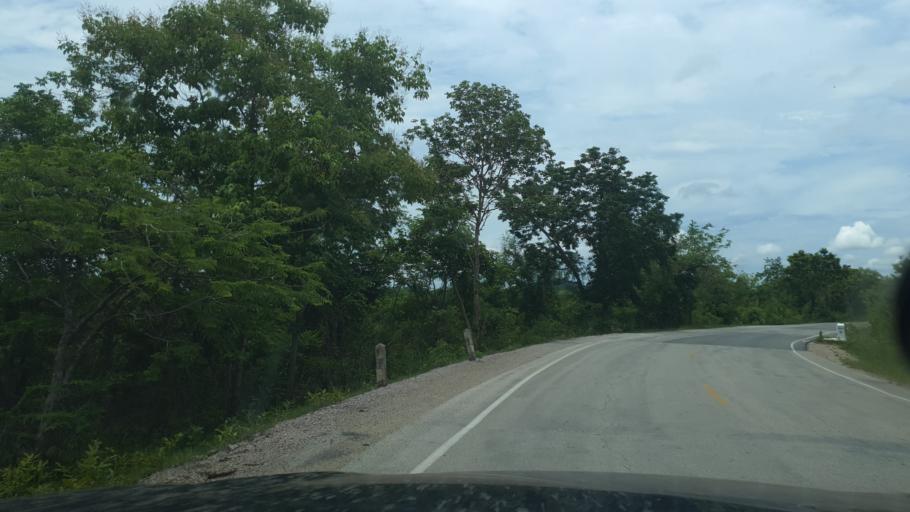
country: TH
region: Lampang
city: Sop Prap
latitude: 17.9165
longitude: 99.4009
